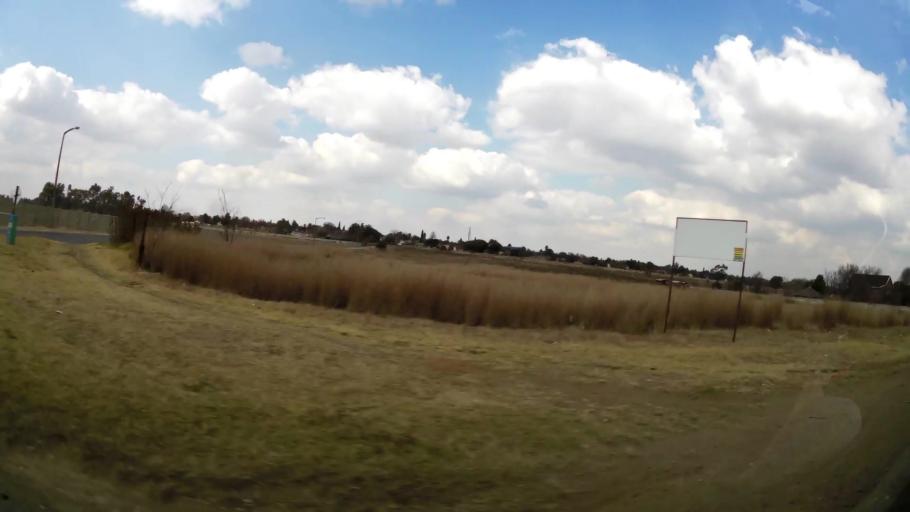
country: ZA
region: Gauteng
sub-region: Ekurhuleni Metropolitan Municipality
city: Benoni
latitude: -26.1209
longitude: 28.3595
